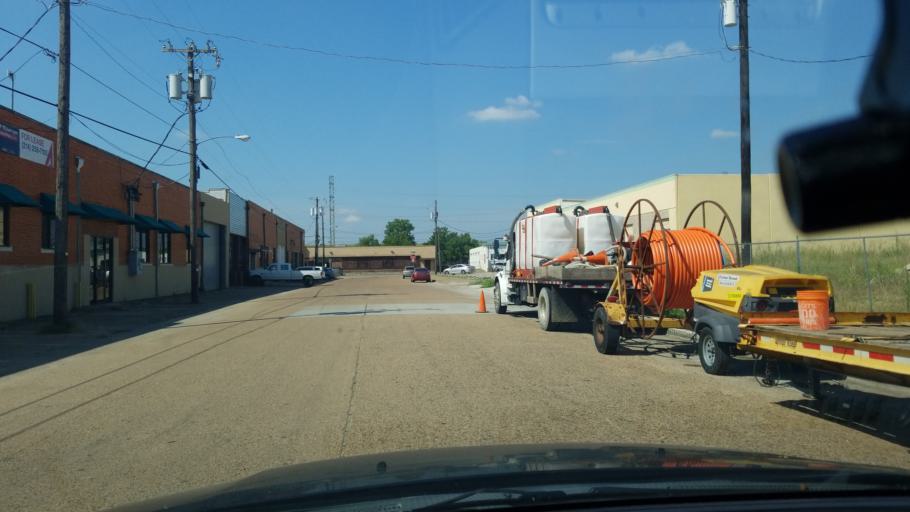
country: US
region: Texas
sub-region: Dallas County
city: Dallas
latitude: 32.7916
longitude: -96.8258
